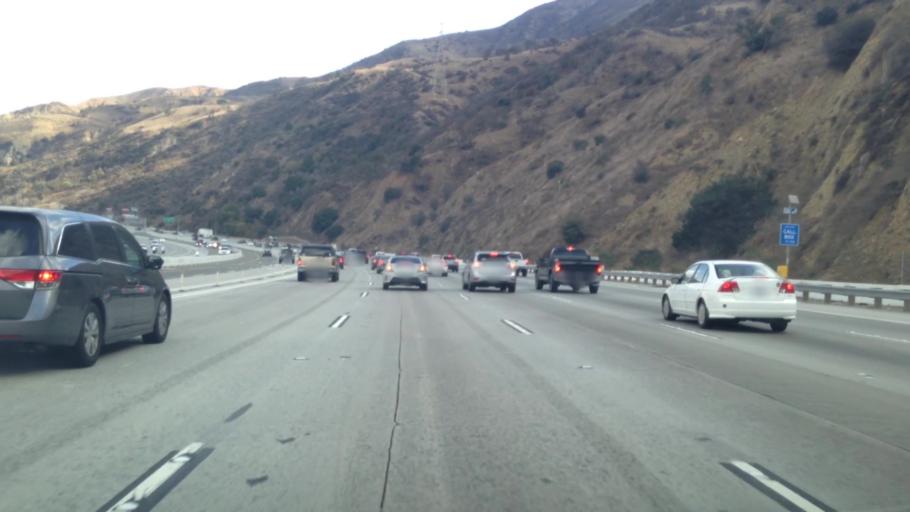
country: US
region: California
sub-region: San Bernardino County
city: Los Serranos
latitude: 33.8693
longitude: -117.6808
